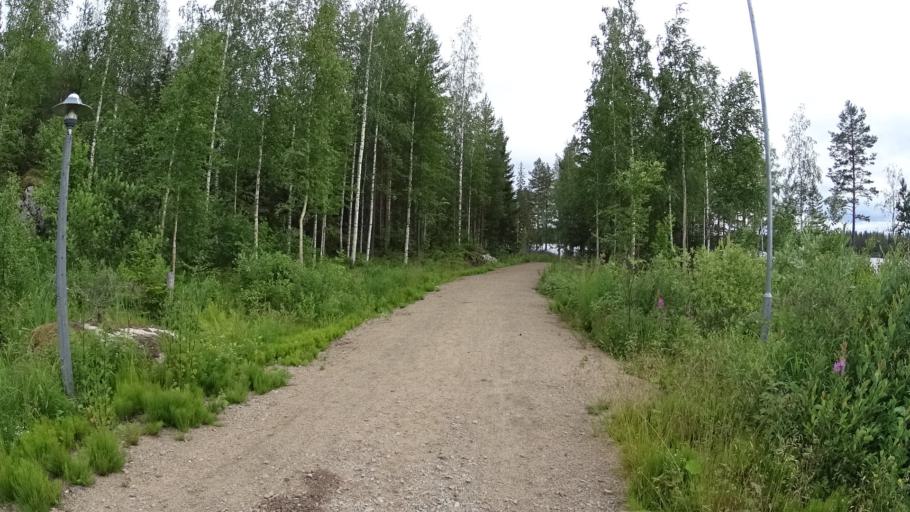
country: FI
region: Southern Ostrobothnia
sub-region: Kuusiokunnat
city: AEhtaeri
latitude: 62.5319
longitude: 24.1872
